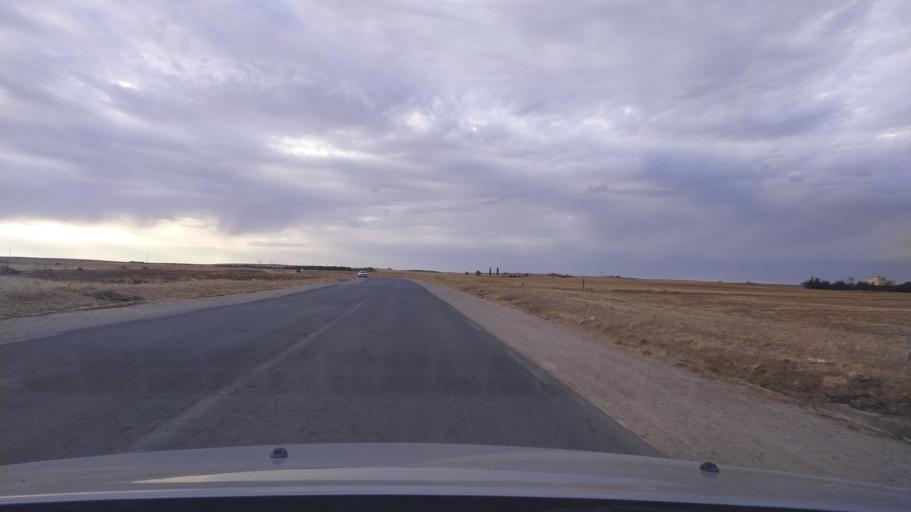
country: DZ
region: Tiaret
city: Frenda
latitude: 34.9795
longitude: 1.1516
